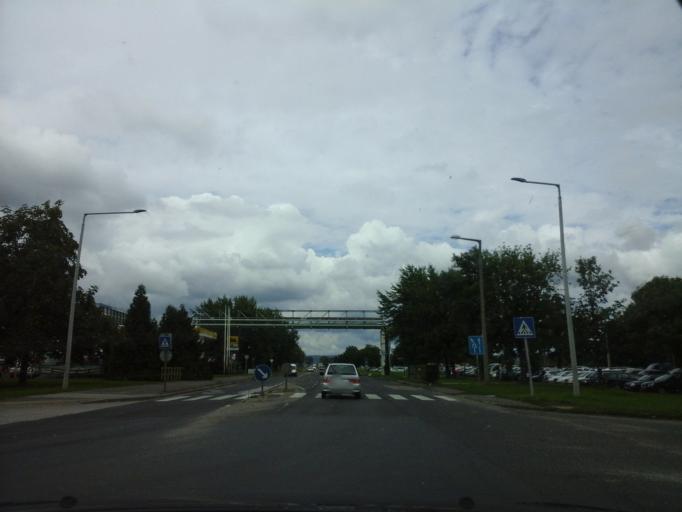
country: HU
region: Borsod-Abauj-Zemplen
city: Kazincbarcika
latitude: 48.2464
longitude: 20.6596
